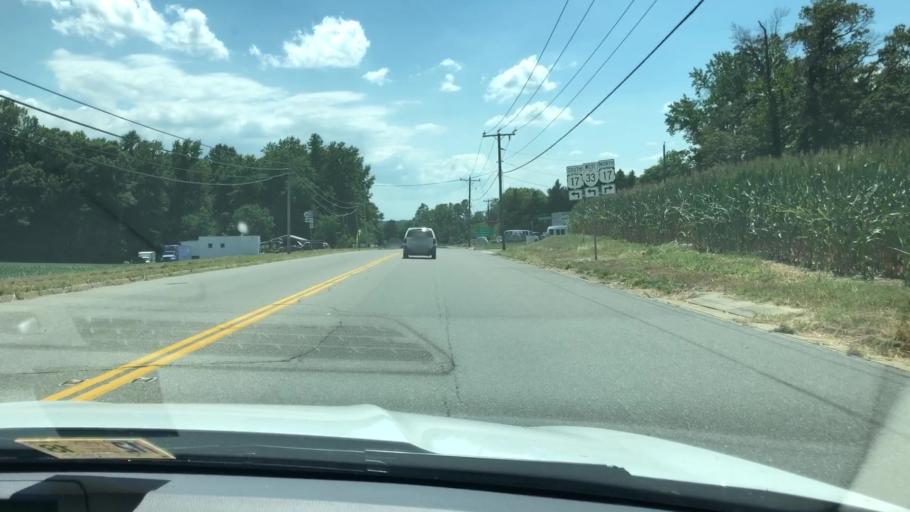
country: US
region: Virginia
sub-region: Middlesex County
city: Saluda
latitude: 37.5993
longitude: -76.6010
